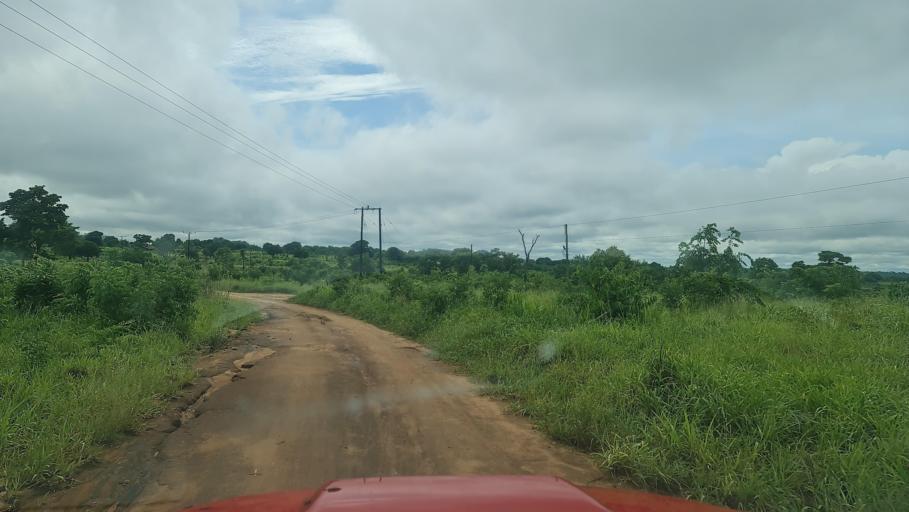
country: MW
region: Southern Region
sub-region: Nsanje District
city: Nsanje
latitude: -17.1851
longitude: 35.9161
